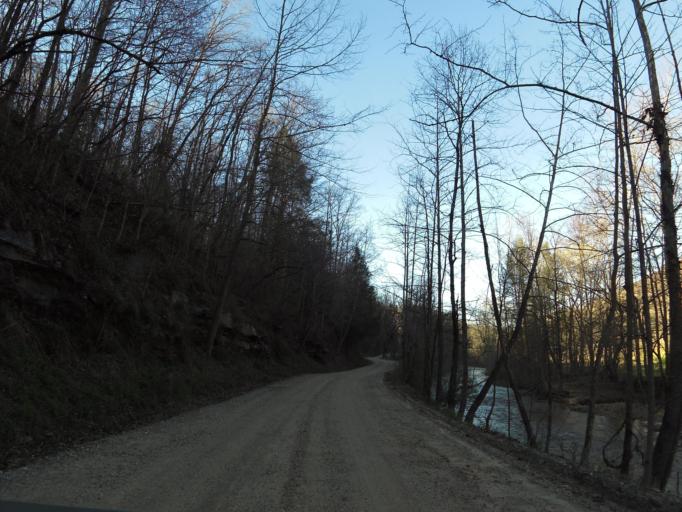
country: US
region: Tennessee
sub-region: Scott County
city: Huntsville
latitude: 36.2340
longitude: -84.4181
